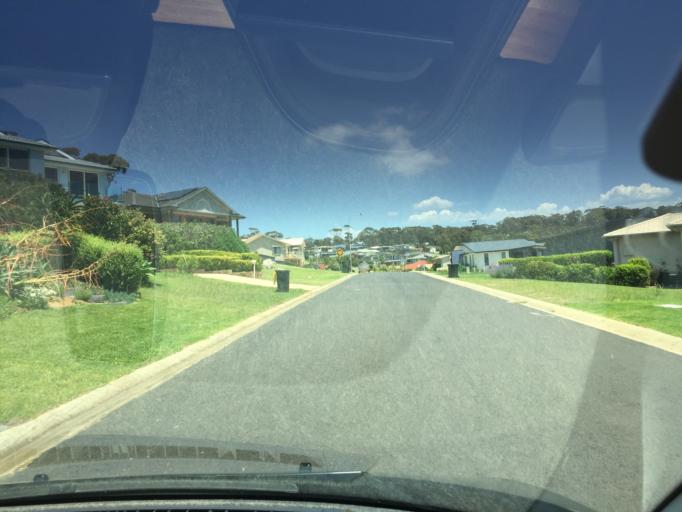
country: AU
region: New South Wales
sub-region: Bega Valley
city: Merimbula
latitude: -36.8501
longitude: 149.9330
